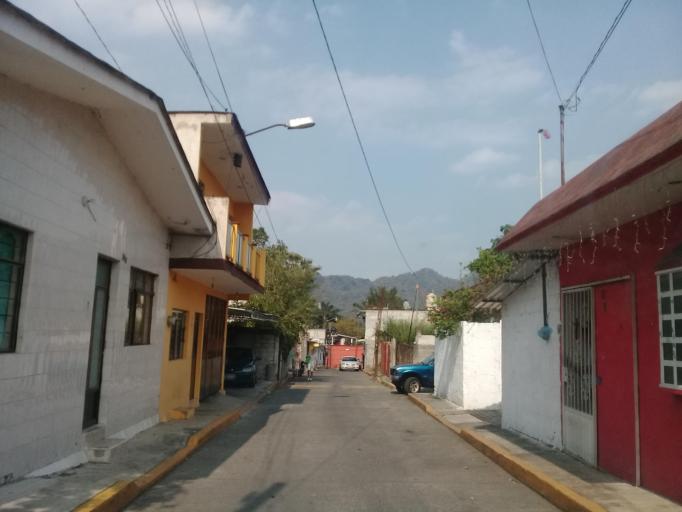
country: MX
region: Veracruz
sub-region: Ixhuatlancillo
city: Union y Progreso
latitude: 18.8697
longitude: -97.1109
